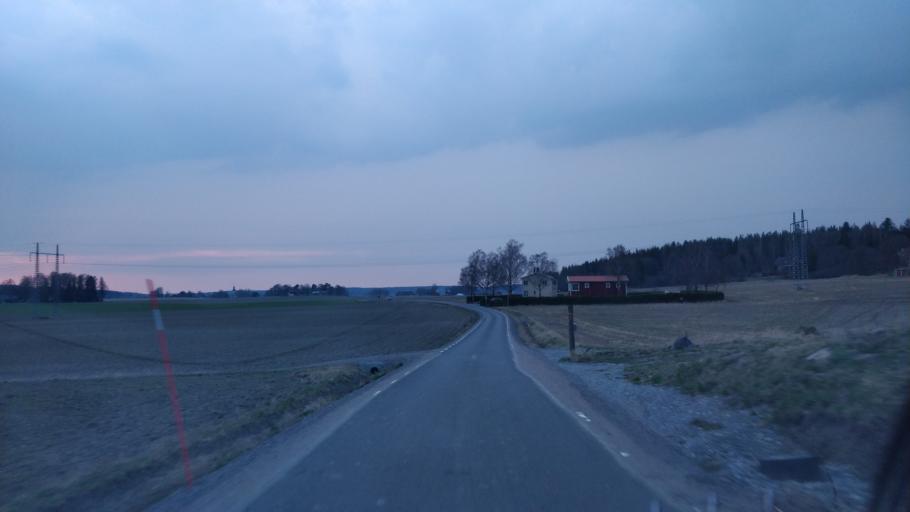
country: SE
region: Uppsala
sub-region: Enkopings Kommun
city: Orsundsbro
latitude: 59.7232
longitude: 17.2244
